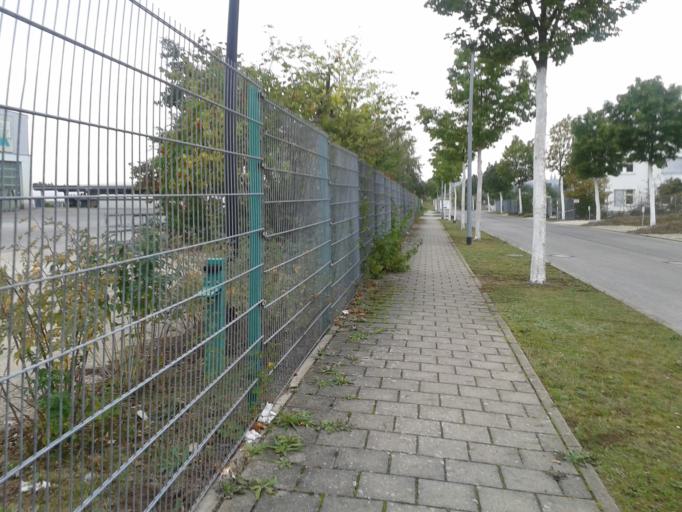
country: DE
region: Bavaria
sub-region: Upper Franconia
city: Hallstadt
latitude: 49.9191
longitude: 10.8908
